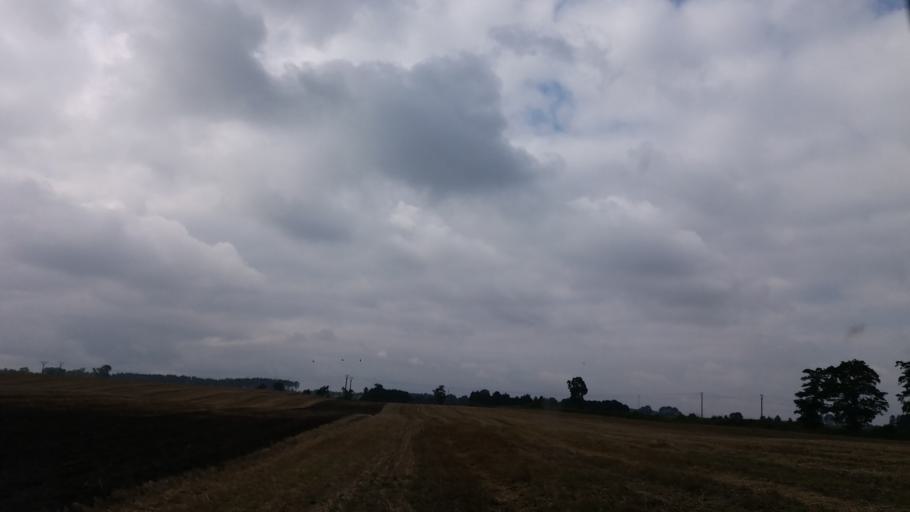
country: PL
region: West Pomeranian Voivodeship
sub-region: Powiat choszczenski
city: Krzecin
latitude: 53.1002
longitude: 15.4930
